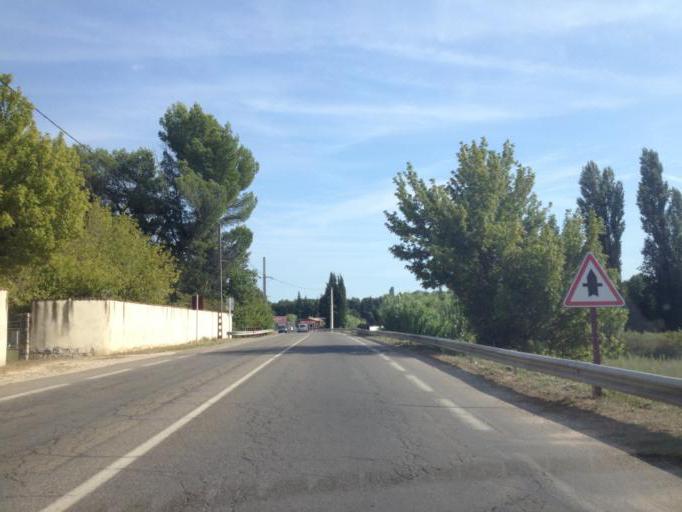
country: FR
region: Provence-Alpes-Cote d'Azur
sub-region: Departement du Vaucluse
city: Aubignan
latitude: 44.0877
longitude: 5.0328
